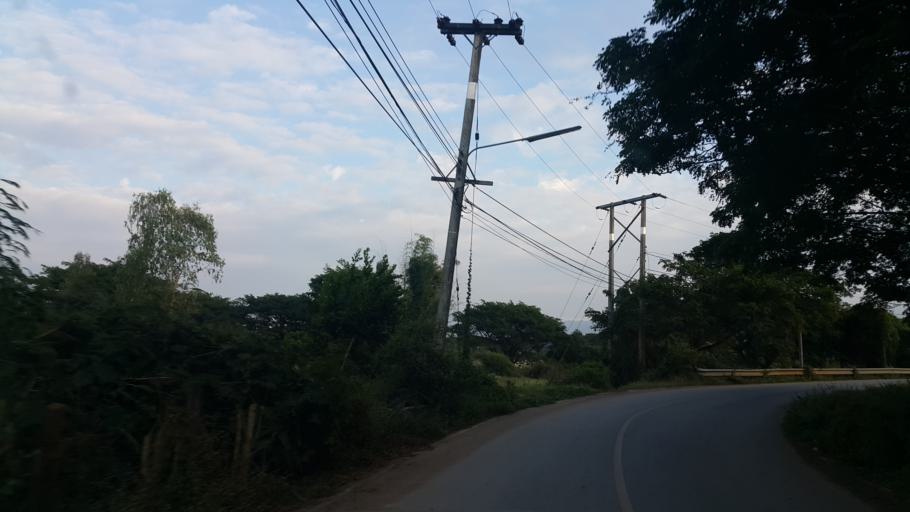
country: TH
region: Lampang
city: Sop Prap
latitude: 17.8974
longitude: 99.3316
